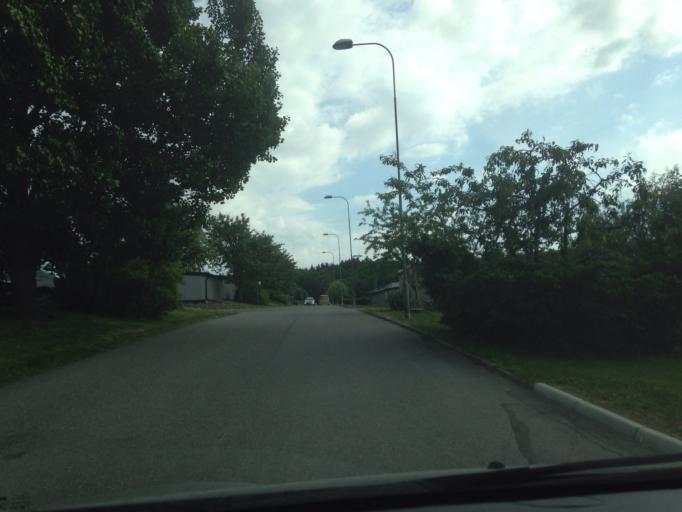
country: SE
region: Vaestra Goetaland
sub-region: Goteborg
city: Majorna
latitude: 57.7492
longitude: 11.9194
